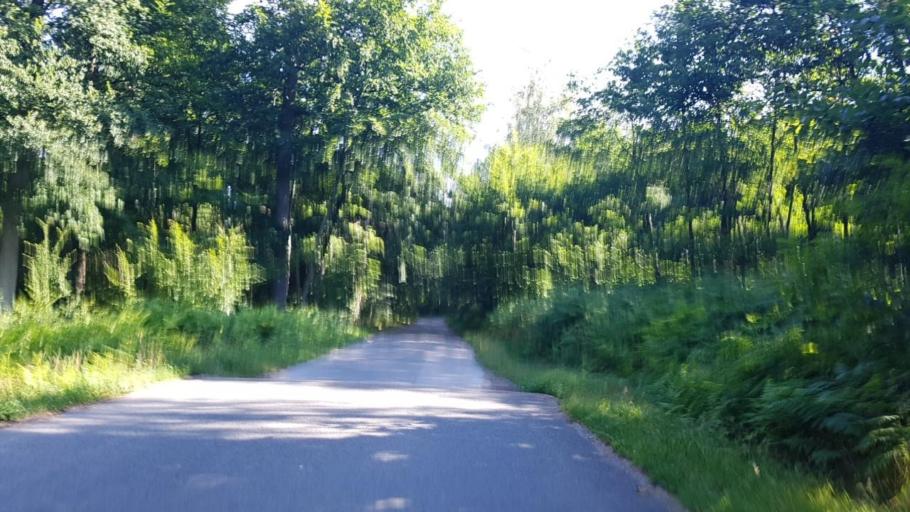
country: FR
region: Picardie
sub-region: Departement de l'Oise
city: Pont-Sainte-Maxence
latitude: 49.2784
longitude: 2.6224
